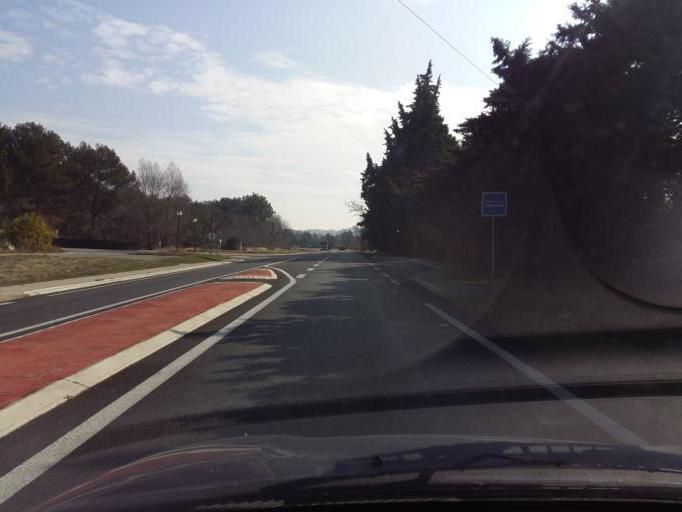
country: FR
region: Provence-Alpes-Cote d'Azur
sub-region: Departement des Bouches-du-Rhone
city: Orgon
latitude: 43.7975
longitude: 5.0107
